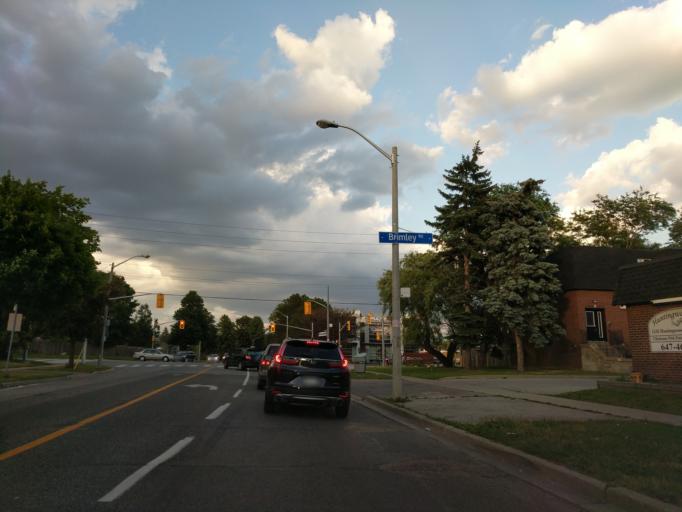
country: CA
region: Ontario
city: Scarborough
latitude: 43.7982
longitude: -79.2742
